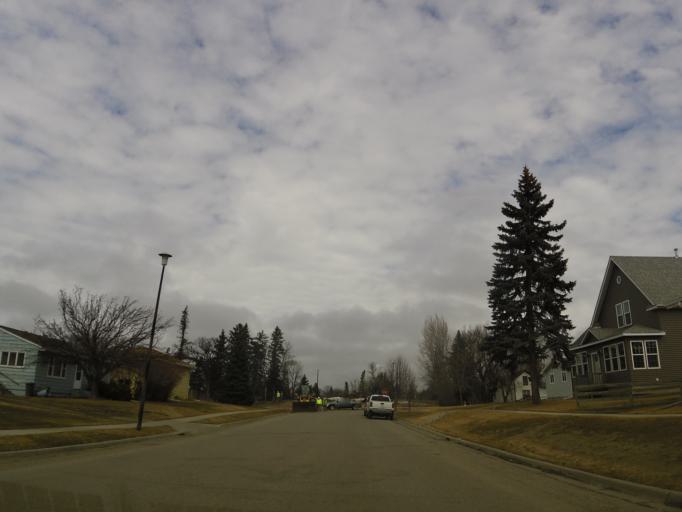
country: US
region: North Dakota
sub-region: Walsh County
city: Grafton
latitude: 48.4189
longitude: -97.4172
